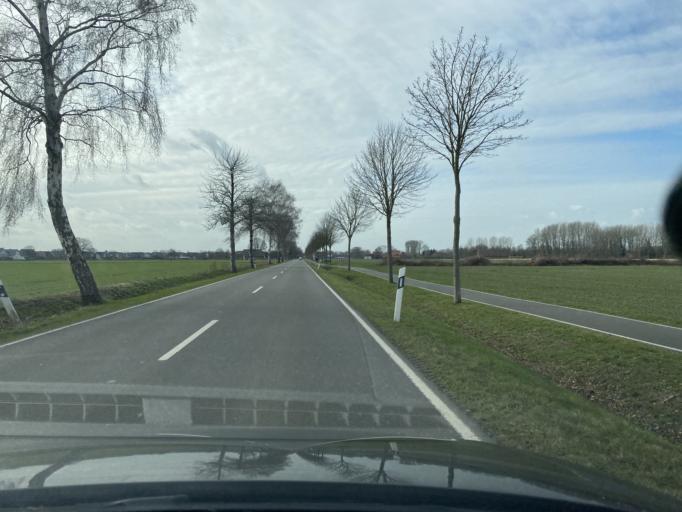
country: DE
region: North Rhine-Westphalia
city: Oelde
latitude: 51.8313
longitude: 8.1730
